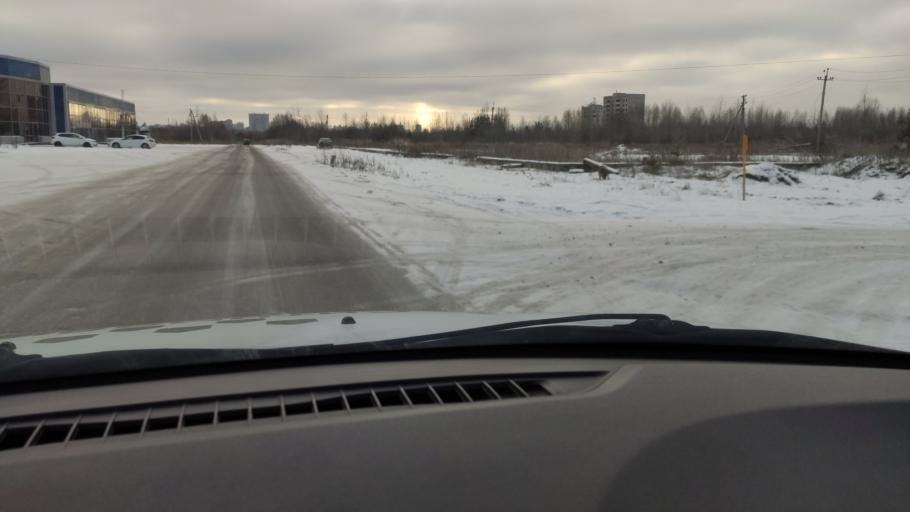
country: RU
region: Perm
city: Perm
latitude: 58.0374
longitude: 56.1902
